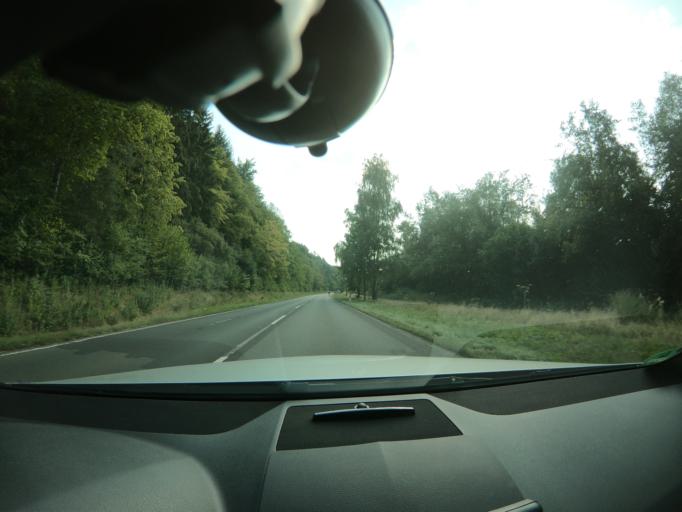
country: DE
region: Hesse
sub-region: Regierungsbezirk Giessen
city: Rauschenberg
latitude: 50.8704
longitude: 8.9364
